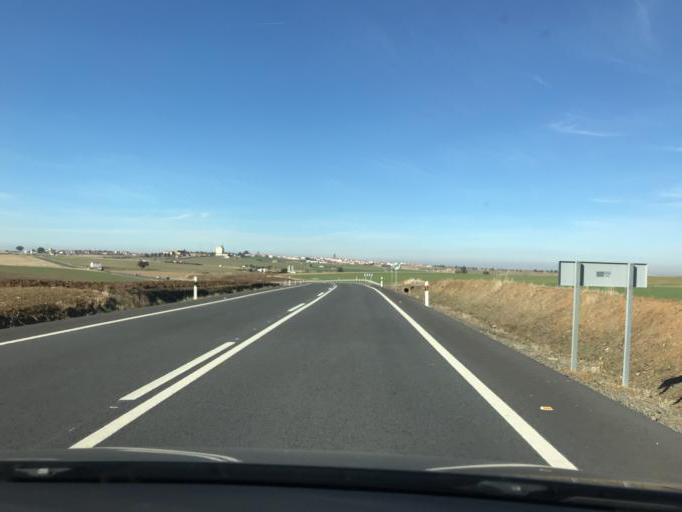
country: ES
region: Extremadura
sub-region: Provincia de Badajoz
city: Granja de Torrehermosa
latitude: 38.3009
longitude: -5.5688
